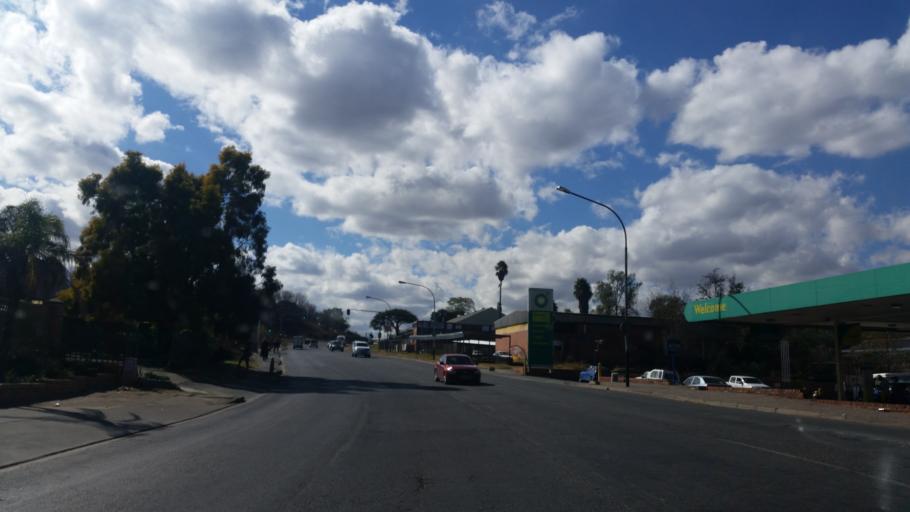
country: ZA
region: KwaZulu-Natal
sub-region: uThukela District Municipality
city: Ladysmith
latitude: -28.5515
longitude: 29.7897
